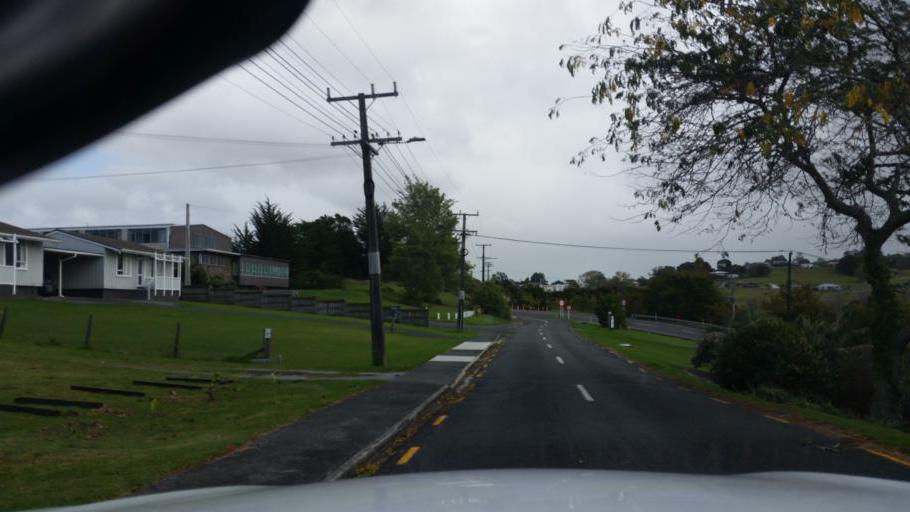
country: NZ
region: Northland
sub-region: Whangarei
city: Ruakaka
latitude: -36.1063
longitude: 174.3613
